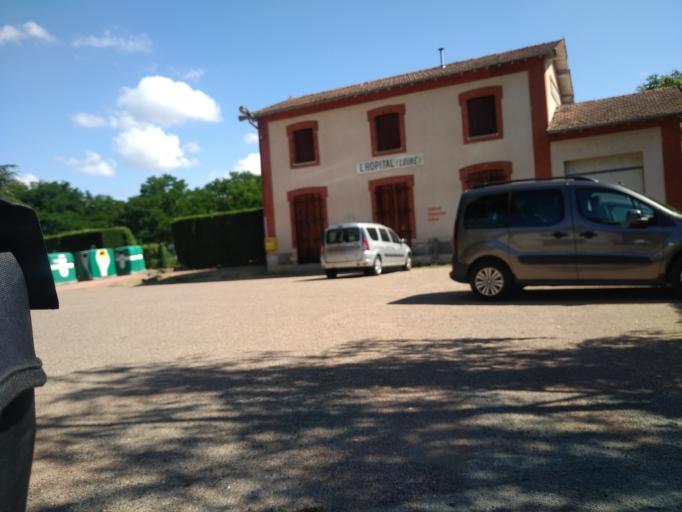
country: FR
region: Rhone-Alpes
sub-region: Departement de la Loire
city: Perreux
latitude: 45.9740
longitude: 4.1316
